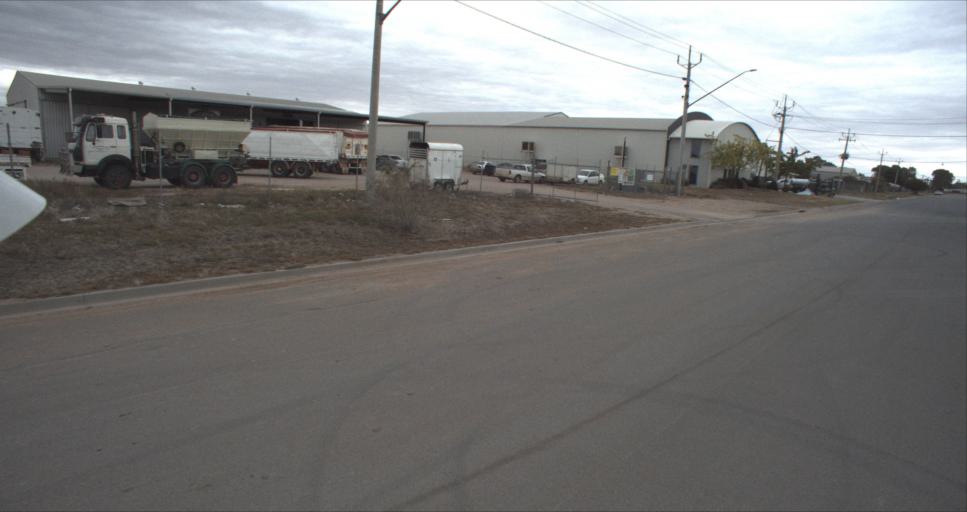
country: AU
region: New South Wales
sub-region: Leeton
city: Leeton
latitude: -34.5457
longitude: 146.3912
